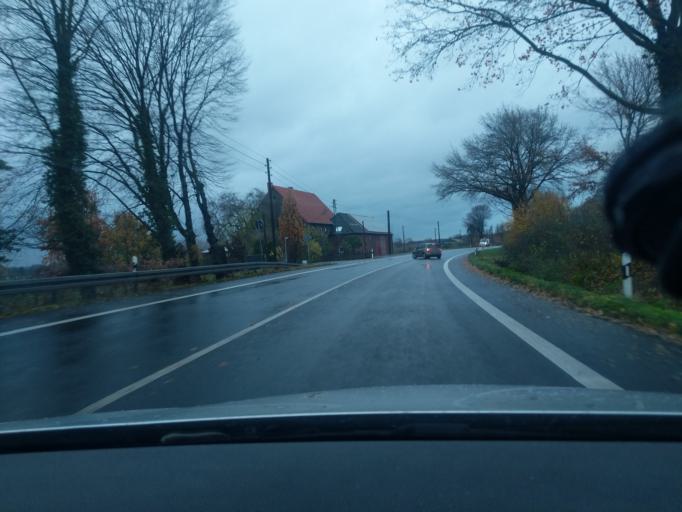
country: DE
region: North Rhine-Westphalia
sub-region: Regierungsbezirk Arnsberg
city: Bonen
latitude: 51.6130
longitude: 7.8046
